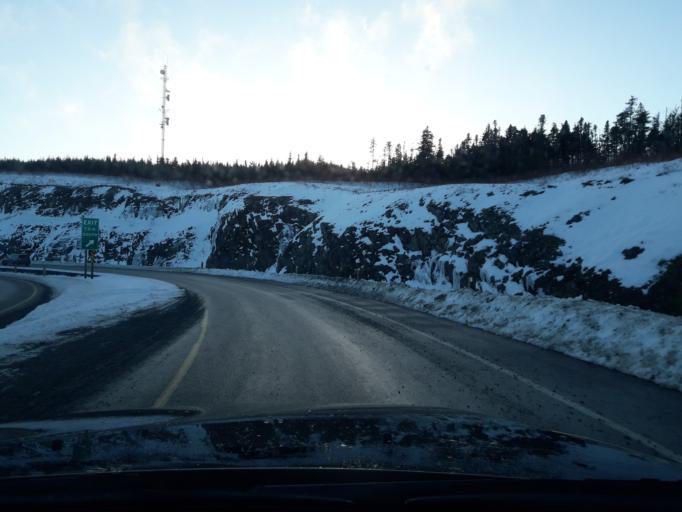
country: CA
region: Newfoundland and Labrador
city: Mount Pearl
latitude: 47.5489
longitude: -52.7659
